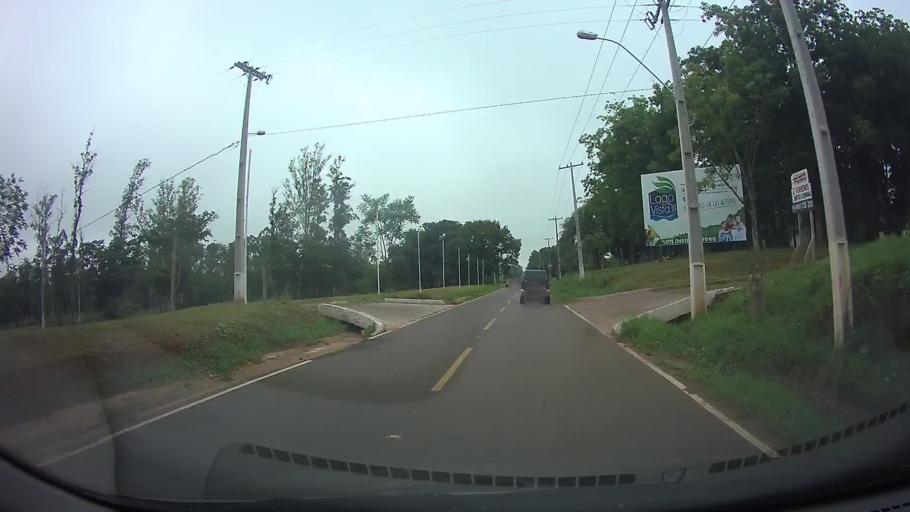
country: PY
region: Central
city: Itaugua
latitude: -25.3611
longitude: -57.3456
